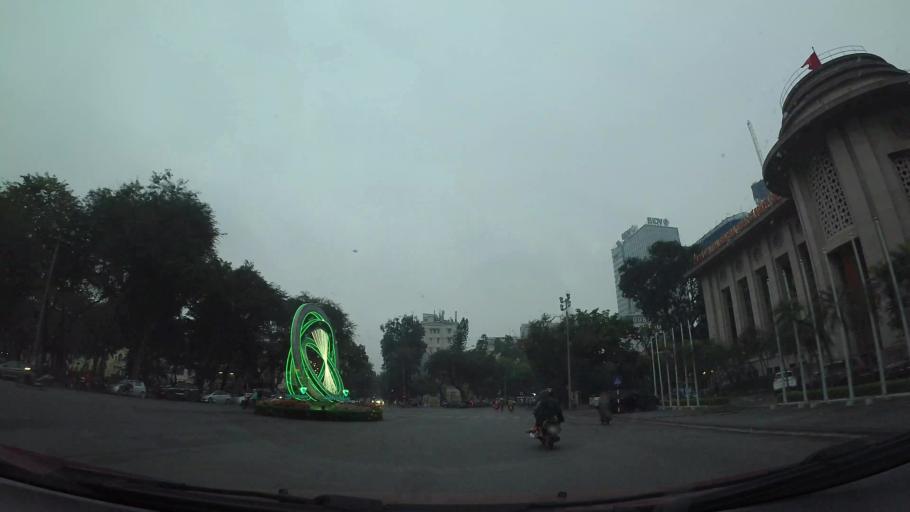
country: VN
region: Ha Noi
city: Hoan Kiem
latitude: 21.0269
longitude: 105.8562
